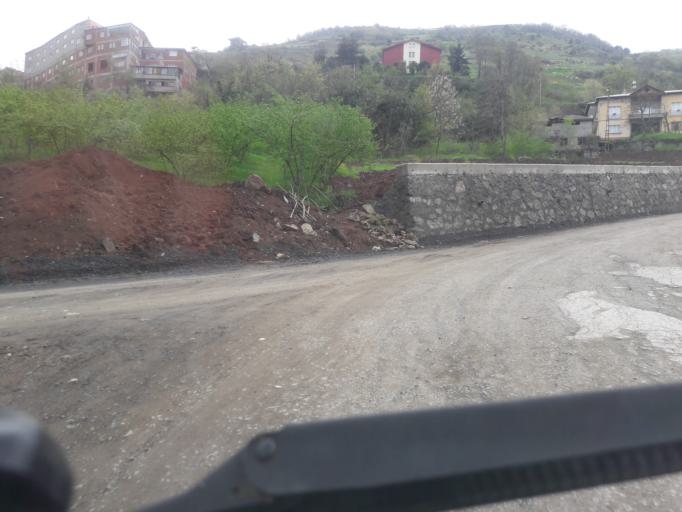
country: TR
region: Trabzon
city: Derecik
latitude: 40.9445
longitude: 39.4990
